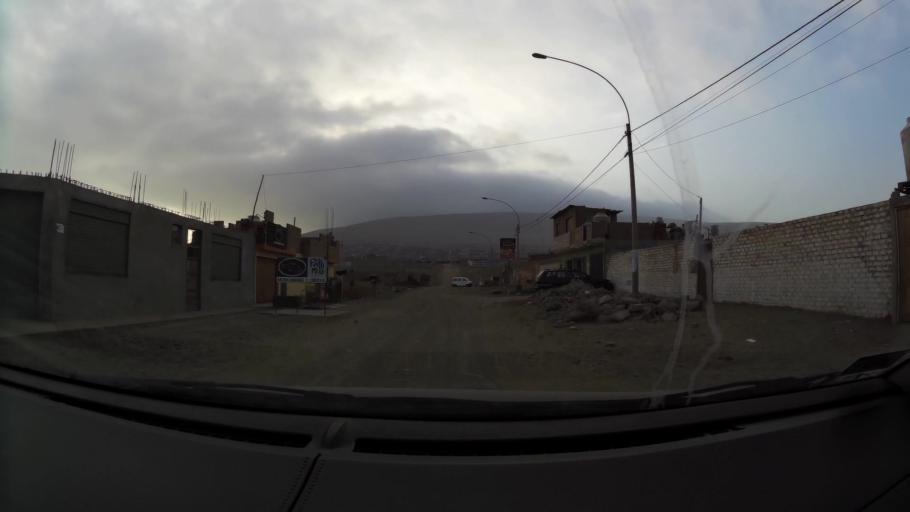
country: PE
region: Lima
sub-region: Lima
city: Santa Rosa
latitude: -11.7373
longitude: -77.1389
